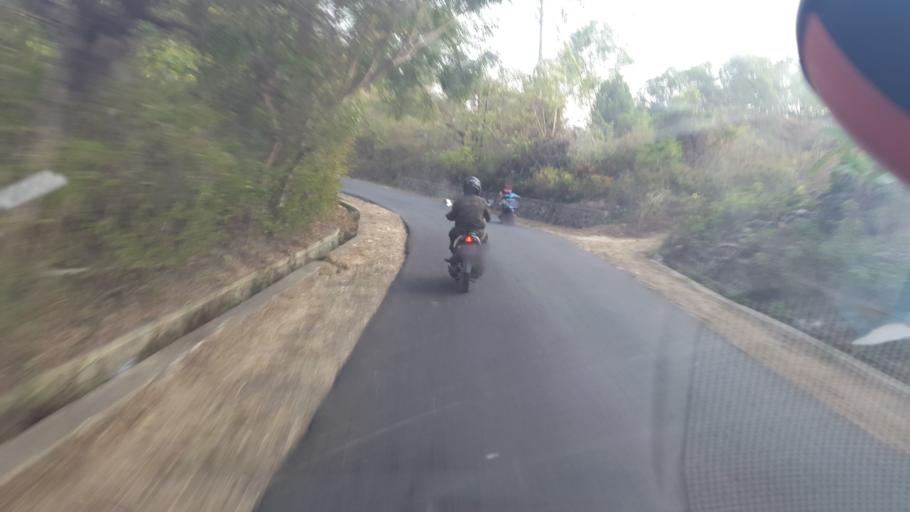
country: ID
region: West Java
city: Pondokaso
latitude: -7.3482
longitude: 106.5326
